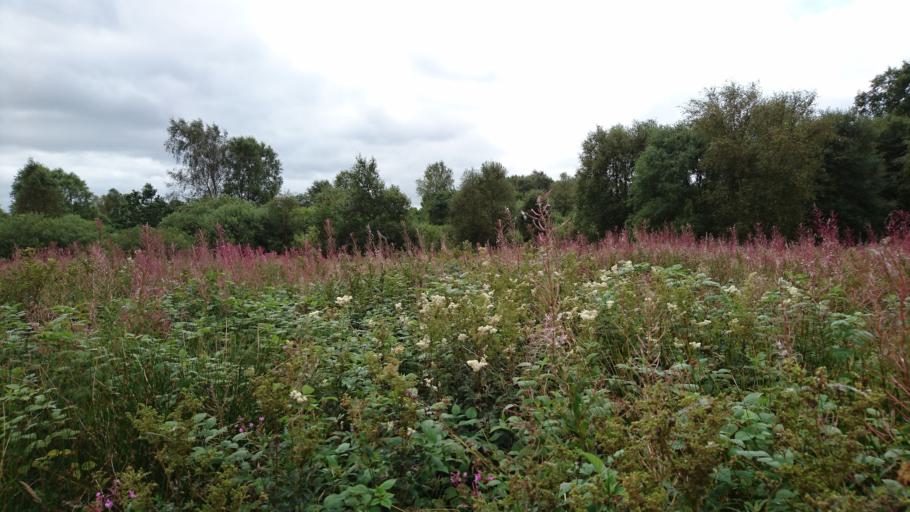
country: DK
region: North Denmark
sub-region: Mariagerfjord Kommune
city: Arden
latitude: 56.7827
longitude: 9.9159
